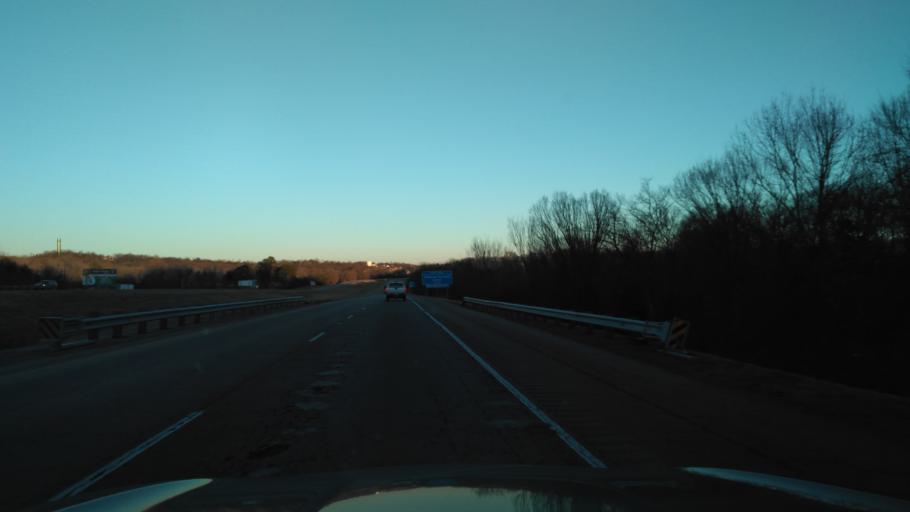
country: US
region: Arkansas
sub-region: Crawford County
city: Van Buren
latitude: 35.4622
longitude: -94.4192
